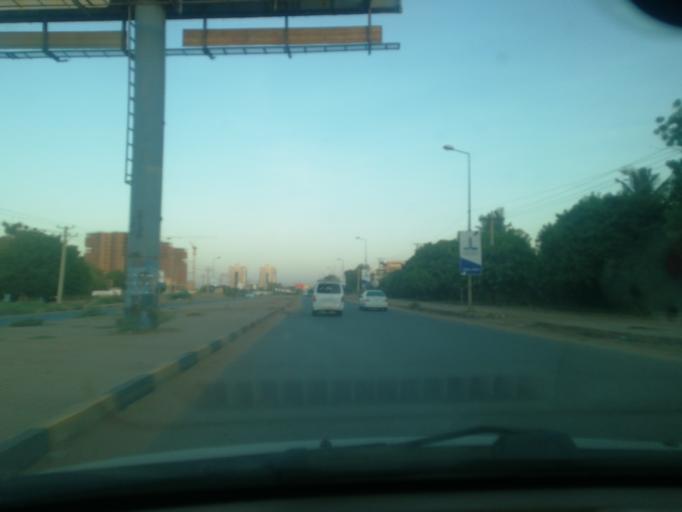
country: SD
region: Khartoum
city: Khartoum
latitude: 15.6208
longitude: 32.5653
